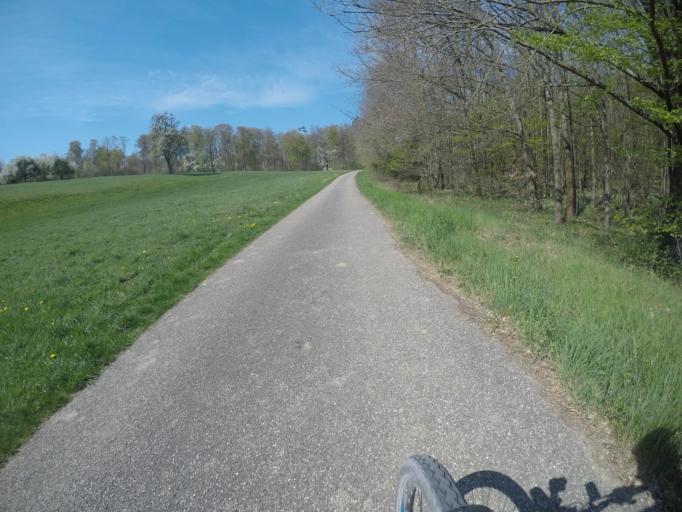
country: DE
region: Baden-Wuerttemberg
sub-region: Regierungsbezirk Stuttgart
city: Rutesheim
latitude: 48.8239
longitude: 8.9653
